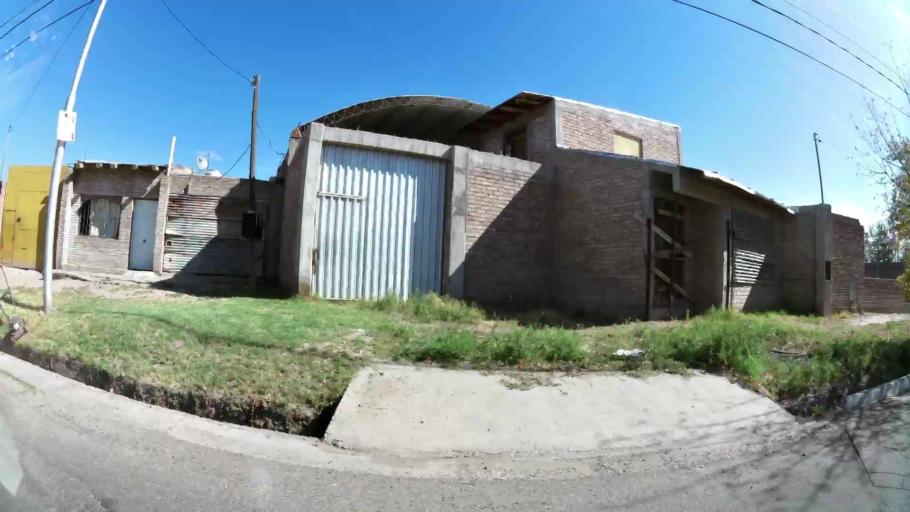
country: AR
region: Mendoza
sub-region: Departamento de Godoy Cruz
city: Godoy Cruz
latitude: -32.9494
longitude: -68.8185
